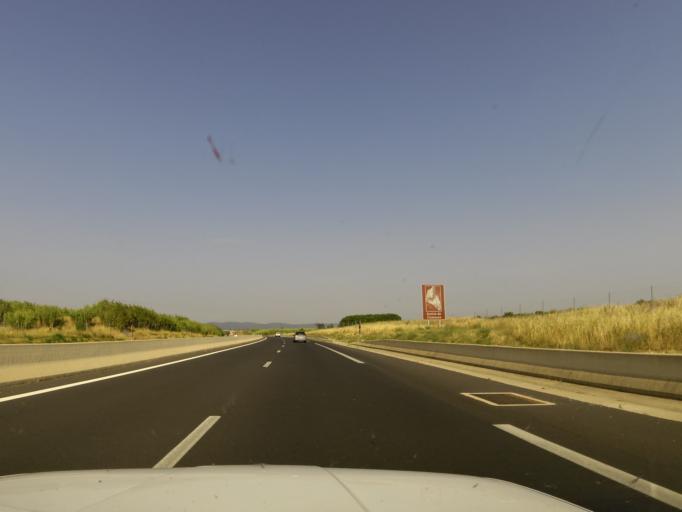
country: FR
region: Languedoc-Roussillon
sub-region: Departement de l'Herault
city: Saint-Andre-de-Sangonis
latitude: 43.6587
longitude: 3.4901
